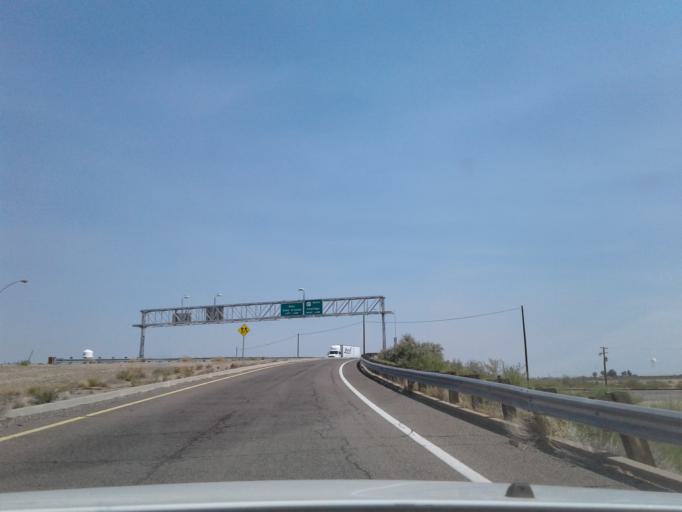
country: US
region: Arizona
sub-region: Pinal County
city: Eloy
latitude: 32.7251
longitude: -111.5152
